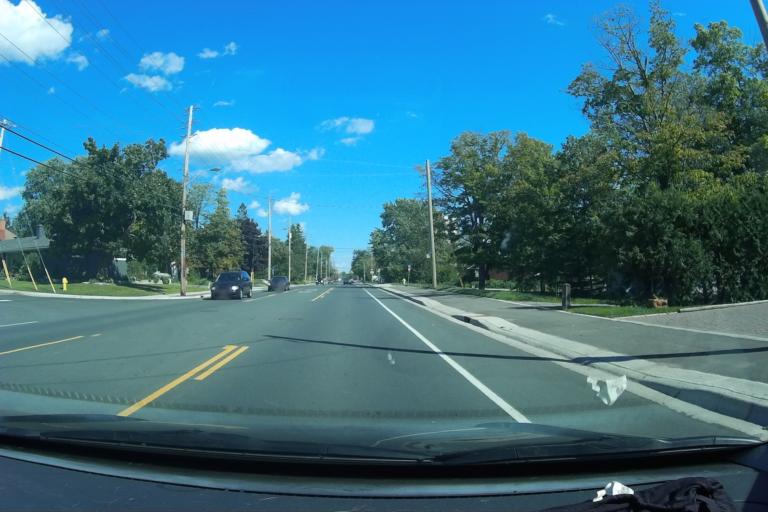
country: CA
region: Ontario
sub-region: Algoma
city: Sault Ste. Marie
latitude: 46.5050
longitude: -84.3119
